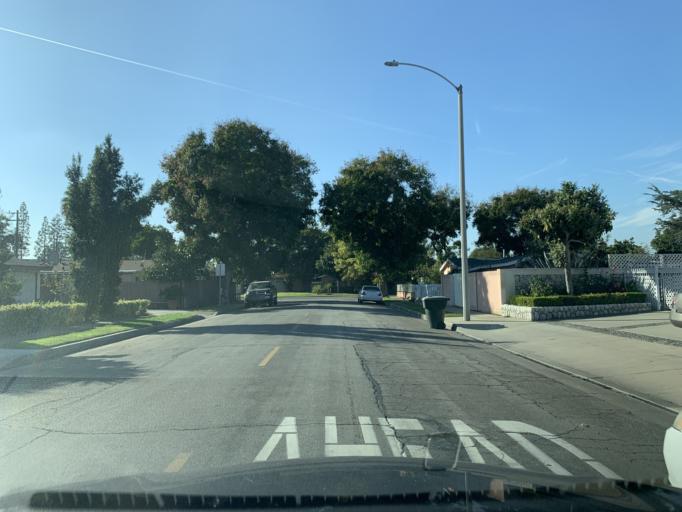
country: US
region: California
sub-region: Orange County
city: Anaheim
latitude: 33.8148
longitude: -117.9127
